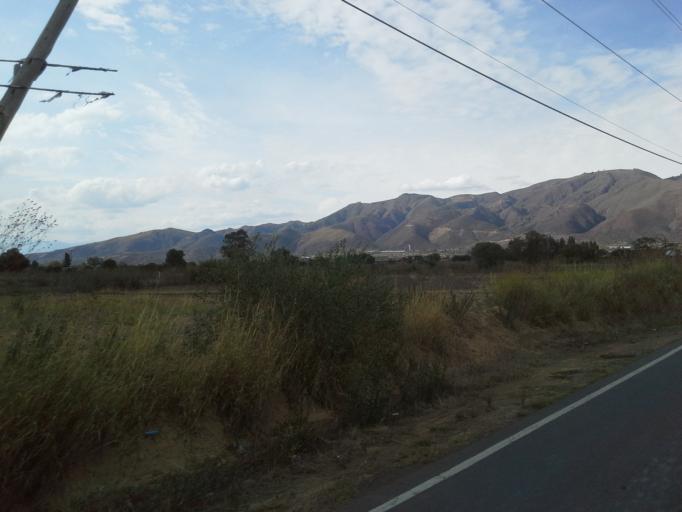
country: BO
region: Cochabamba
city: Tarata
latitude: -17.5690
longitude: -66.0128
